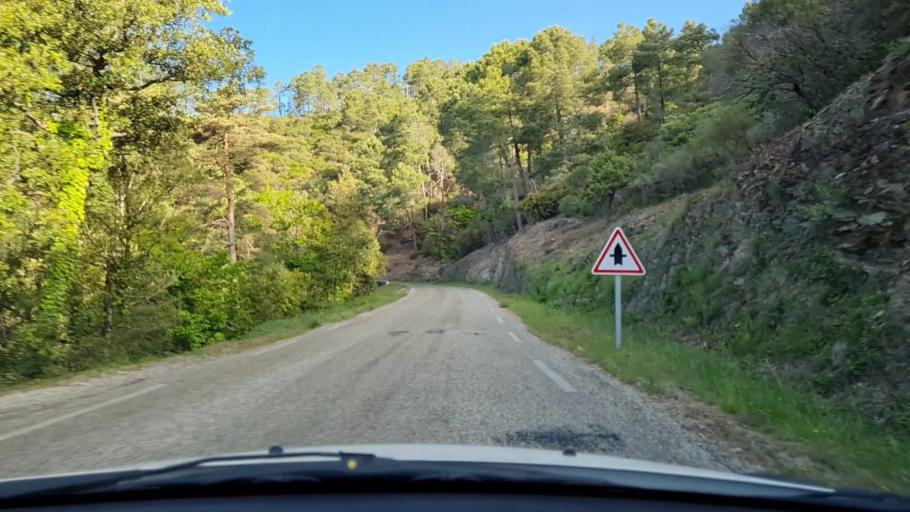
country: FR
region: Languedoc-Roussillon
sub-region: Departement du Gard
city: Branoux-les-Taillades
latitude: 44.1848
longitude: 3.9986
